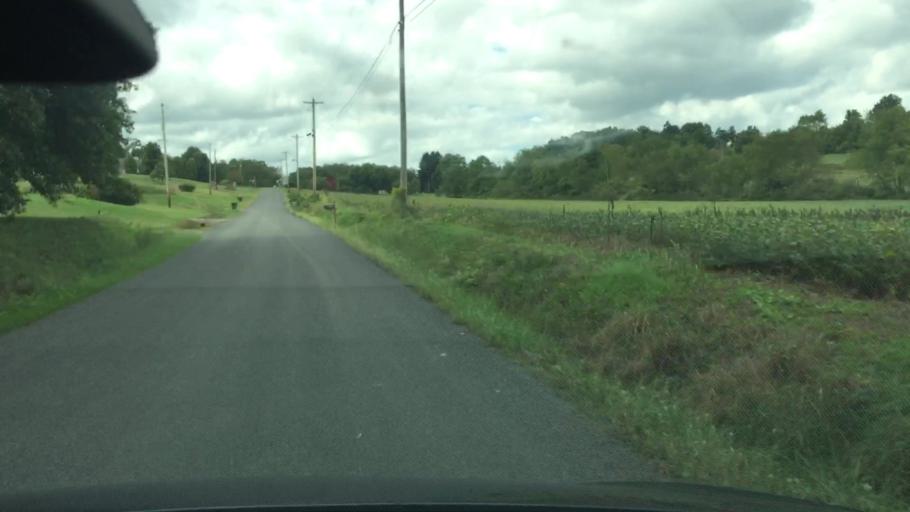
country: US
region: Pennsylvania
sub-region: Butler County
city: Saxonburg
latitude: 40.7305
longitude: -79.8731
